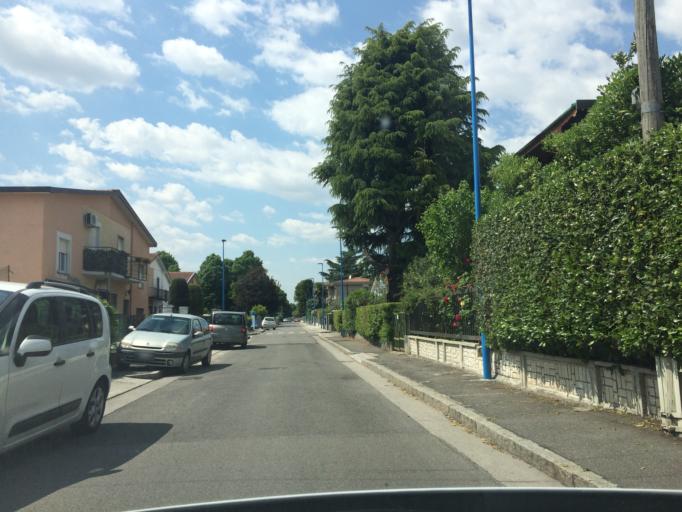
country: IT
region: Lombardy
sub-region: Provincia di Brescia
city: Folzano
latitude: 45.5089
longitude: 10.1902
